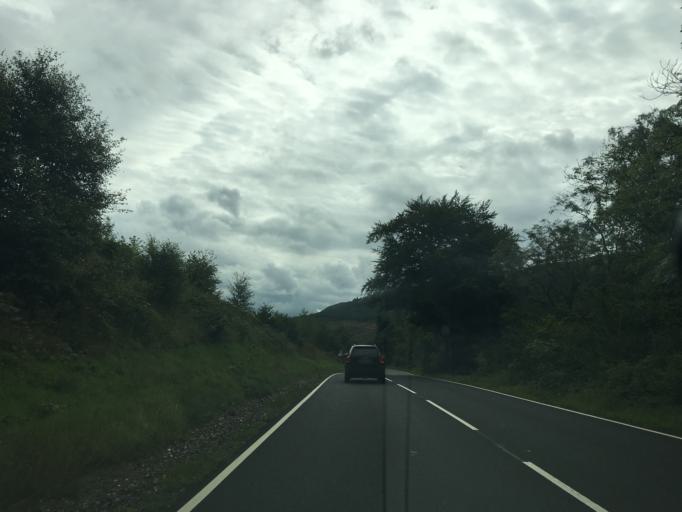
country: GB
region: Scotland
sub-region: Stirling
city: Callander
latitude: 56.2644
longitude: -4.2866
